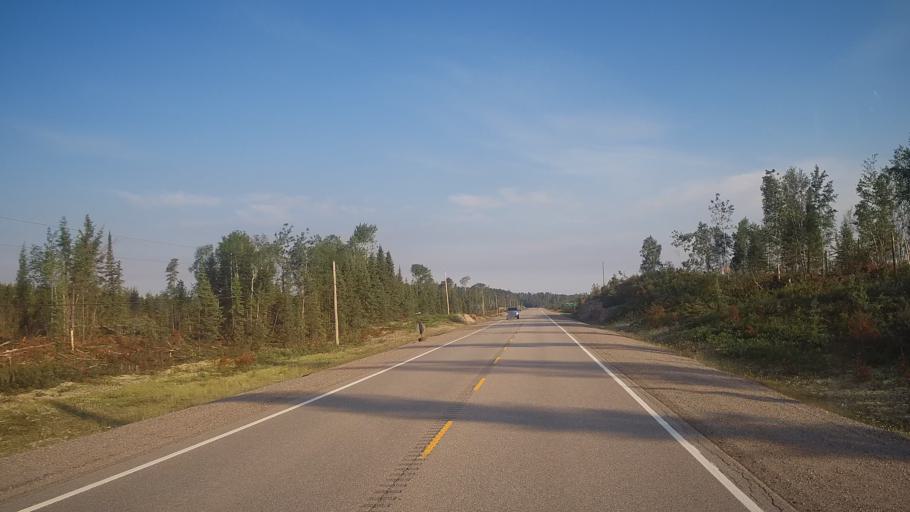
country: CA
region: Ontario
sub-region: Rainy River District
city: Atikokan
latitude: 49.3631
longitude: -91.5469
